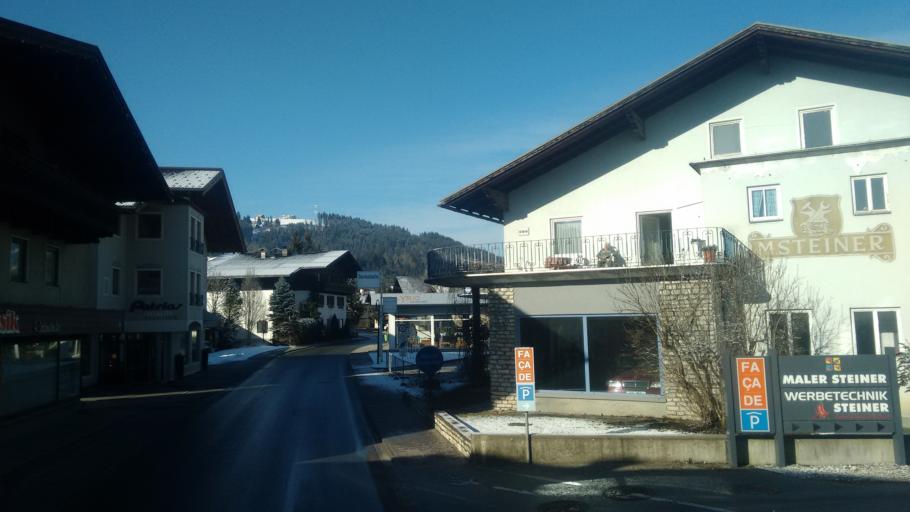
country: AT
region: Salzburg
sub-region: Politischer Bezirk Sankt Johann im Pongau
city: Altenmarkt im Pongau
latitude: 47.3800
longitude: 13.4261
